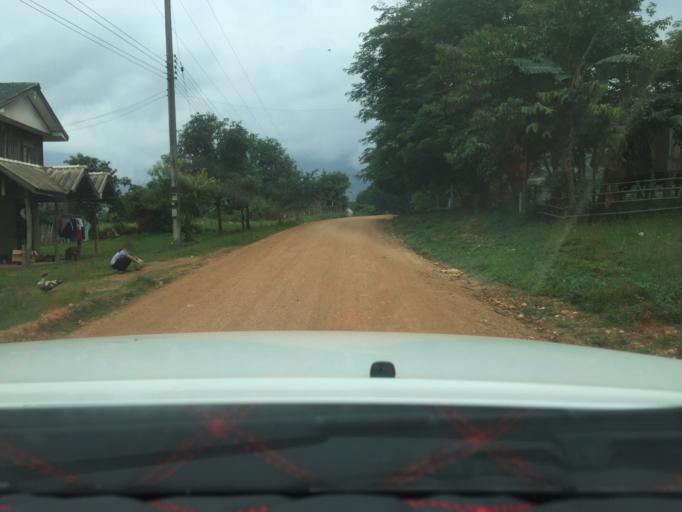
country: TH
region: Phayao
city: Phu Sang
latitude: 19.7387
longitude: 100.4667
